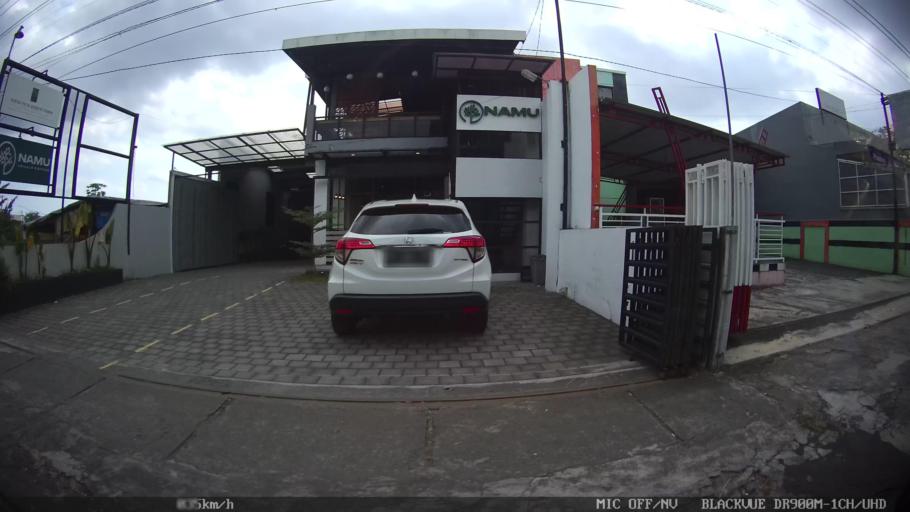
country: ID
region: Daerah Istimewa Yogyakarta
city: Yogyakarta
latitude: -7.7571
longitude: 110.3464
